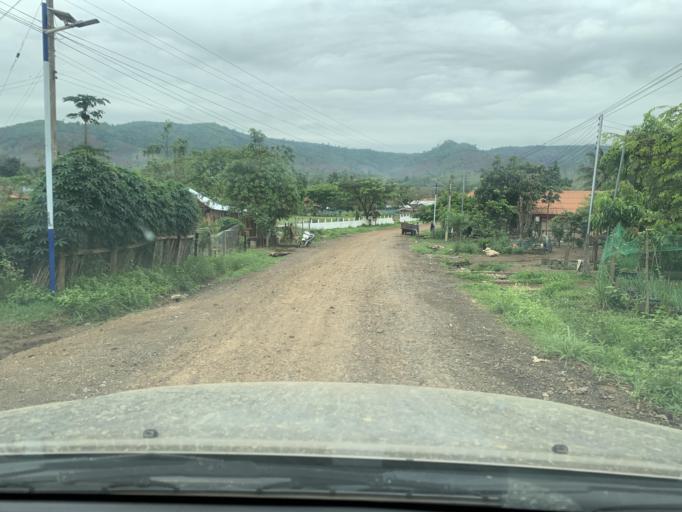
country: TH
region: Nan
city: Mae Charim
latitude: 18.4191
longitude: 101.4516
